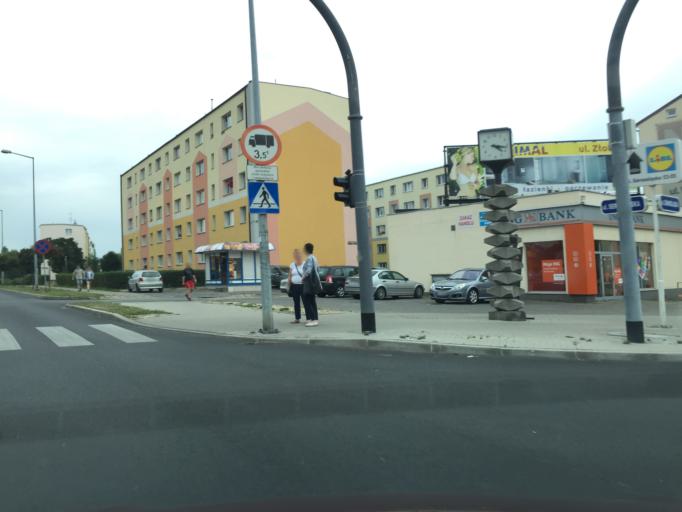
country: PL
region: Greater Poland Voivodeship
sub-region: Kalisz
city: Kalisz
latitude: 51.7474
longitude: 18.0723
